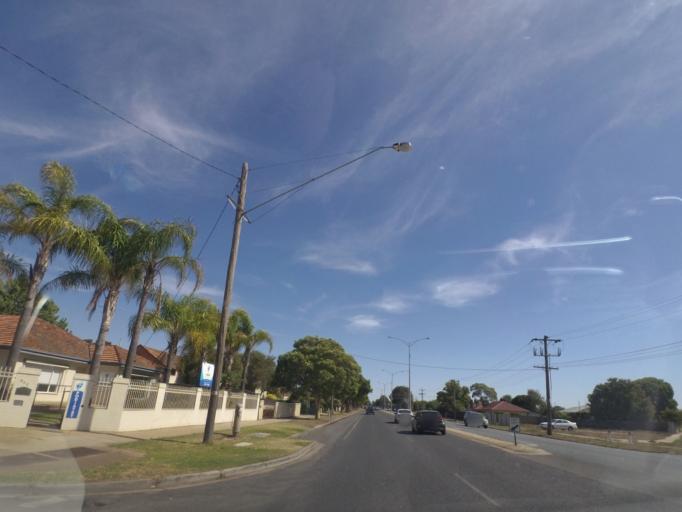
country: AU
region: Victoria
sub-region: Greater Shepparton
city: Shepparton
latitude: -36.3924
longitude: 145.3971
